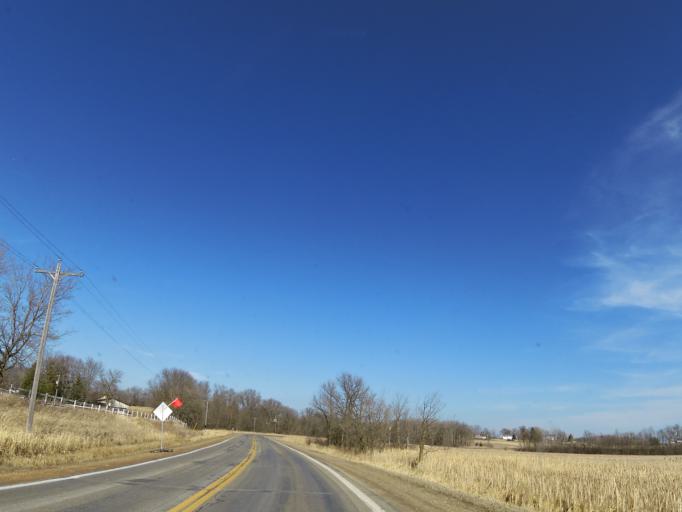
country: US
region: Minnesota
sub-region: Scott County
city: Prior Lake
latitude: 44.6309
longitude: -93.4479
